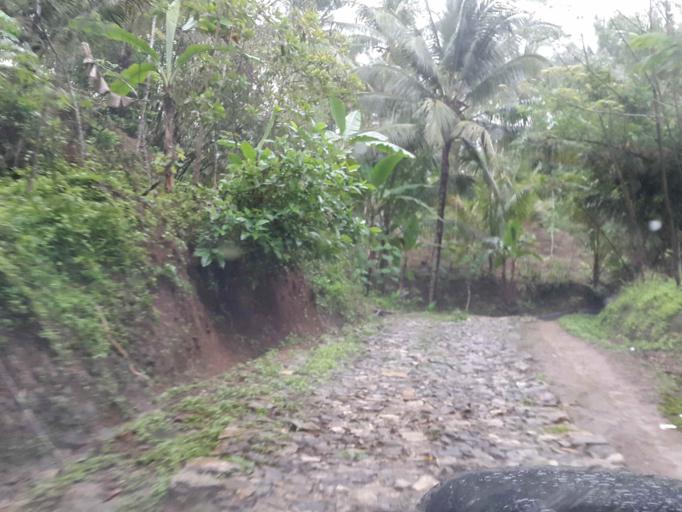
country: ID
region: Central Java
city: Kutoarjo
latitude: -7.5641
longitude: 109.7701
